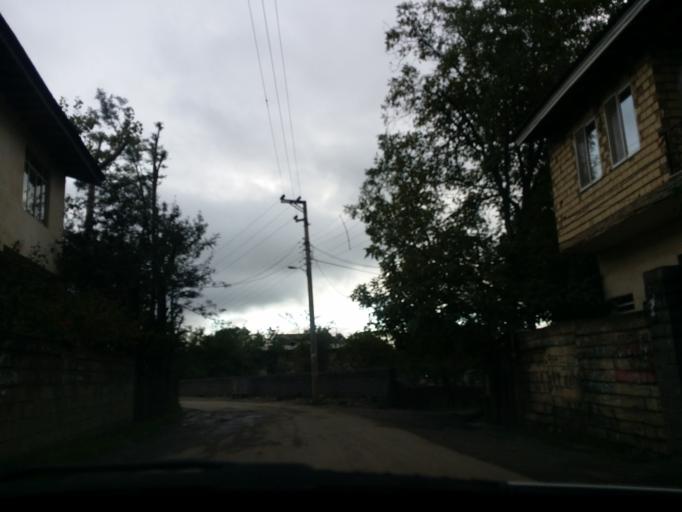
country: IR
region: Mazandaran
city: `Abbasabad
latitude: 36.5068
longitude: 51.1854
